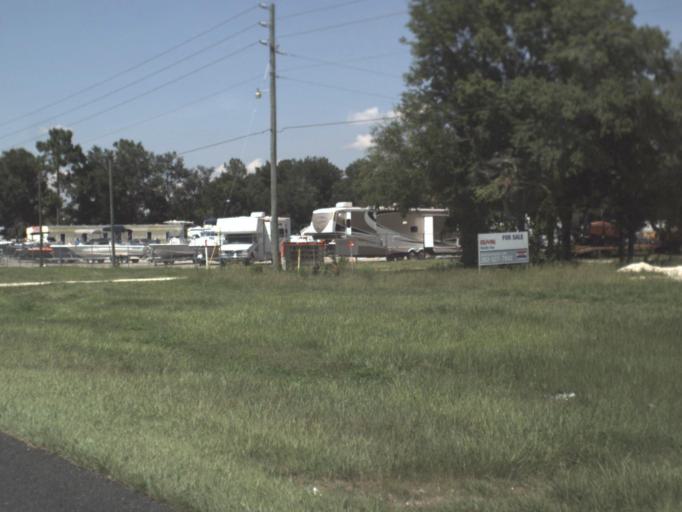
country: US
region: Florida
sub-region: Citrus County
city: Homosassa Springs
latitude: 28.8385
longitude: -82.5794
